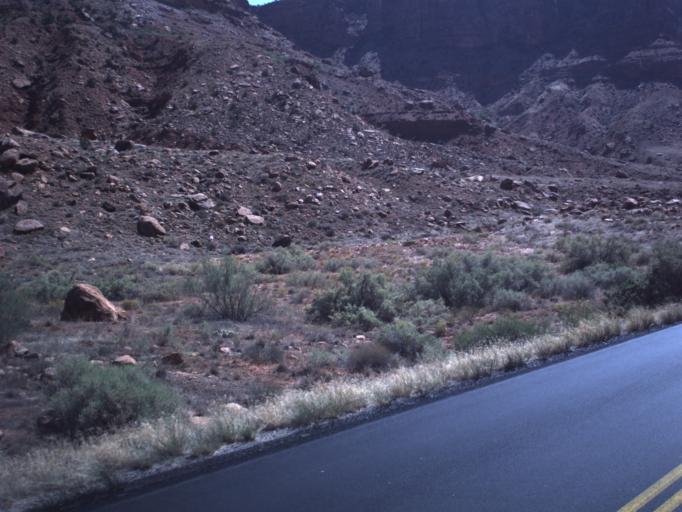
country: US
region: Utah
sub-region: Grand County
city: Moab
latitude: 38.6427
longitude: -109.4763
